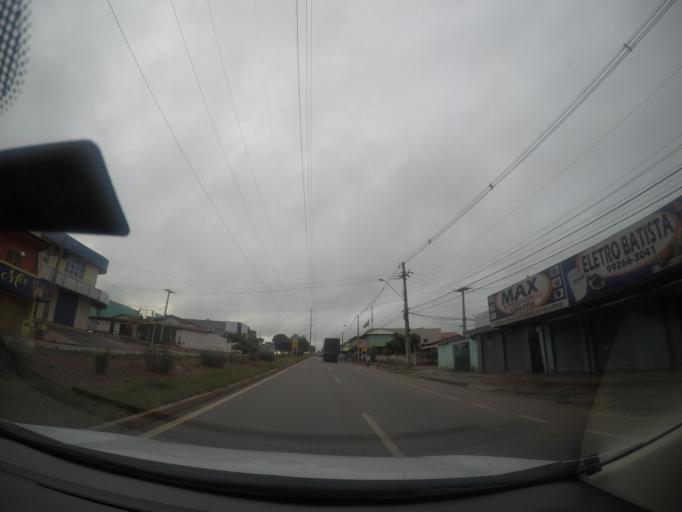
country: BR
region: Goias
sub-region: Aparecida De Goiania
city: Aparecida de Goiania
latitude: -16.7589
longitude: -49.3323
